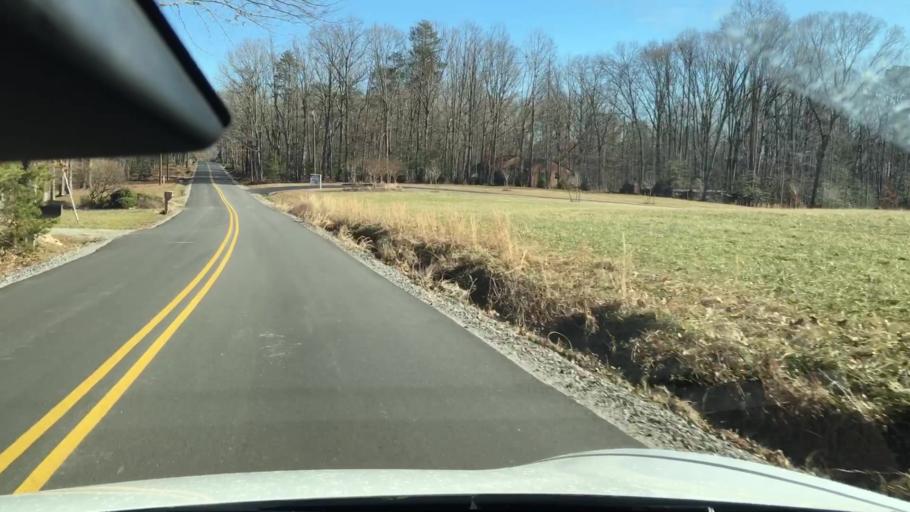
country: US
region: Virginia
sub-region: Powhatan County
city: Powhatan
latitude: 37.5616
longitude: -77.7959
